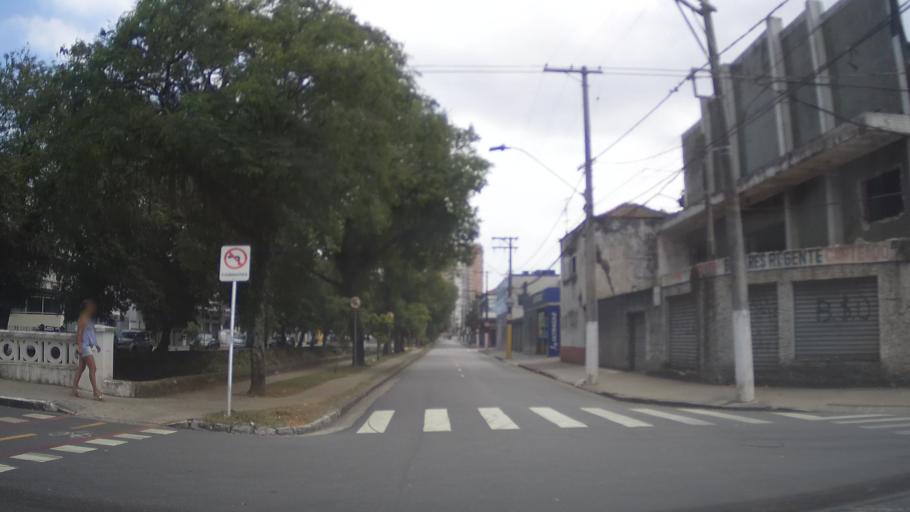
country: BR
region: Sao Paulo
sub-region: Santos
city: Santos
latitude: -23.9605
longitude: -46.3101
